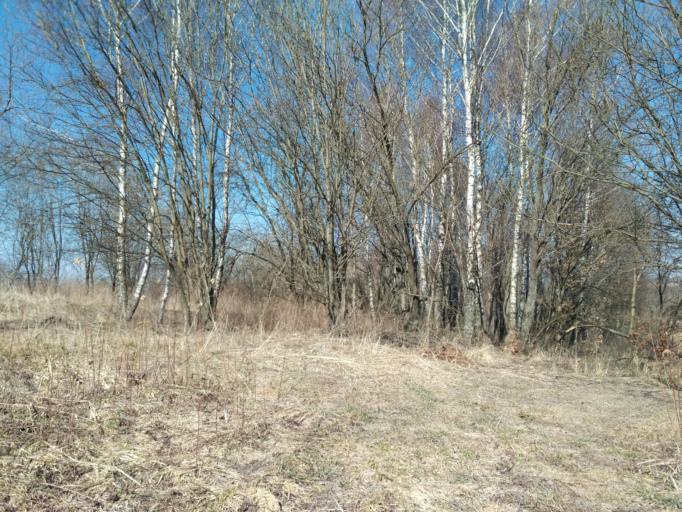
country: PL
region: Subcarpathian Voivodeship
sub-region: Powiat brzozowski
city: Golcowa
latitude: 49.7614
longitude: 22.0315
